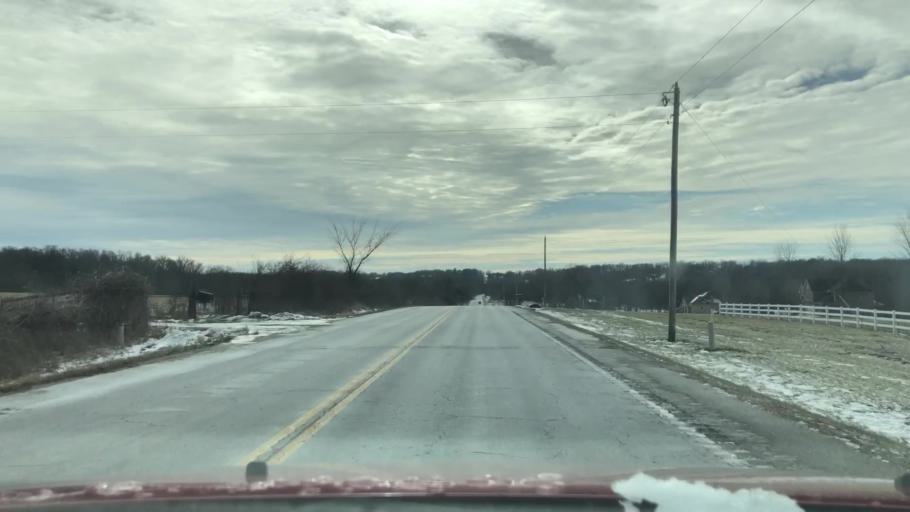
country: US
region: Missouri
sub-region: Jackson County
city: Lone Jack
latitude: 38.9083
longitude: -94.1335
